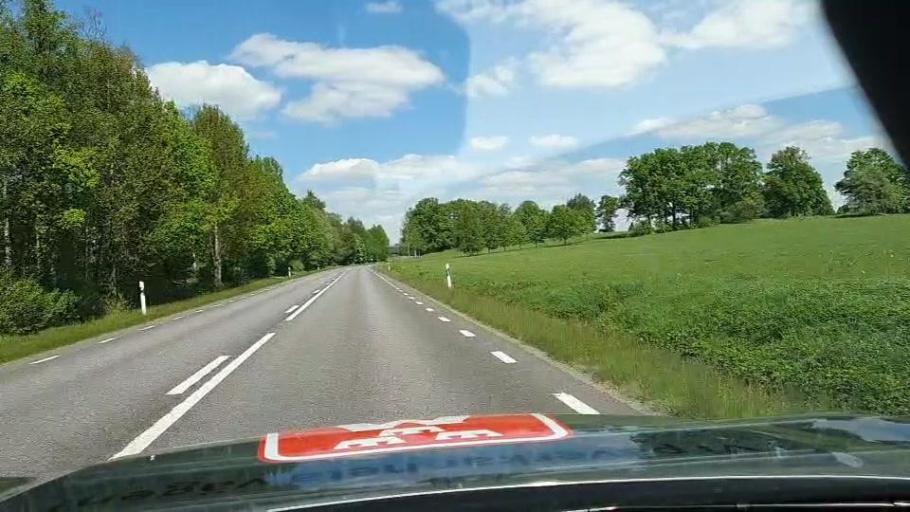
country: SE
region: Kronoberg
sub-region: Alvesta Kommun
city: Moheda
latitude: 57.0316
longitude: 14.5634
